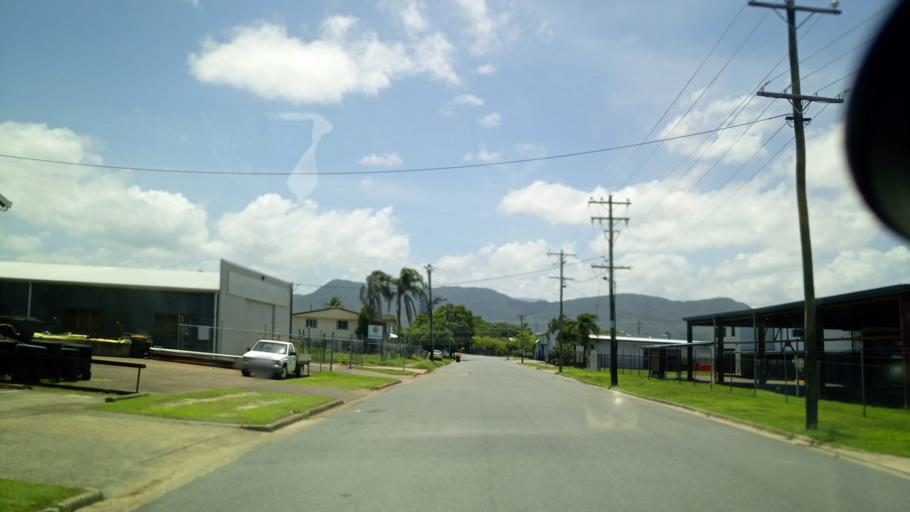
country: AU
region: Queensland
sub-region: Cairns
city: Cairns
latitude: -16.9331
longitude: 145.7634
